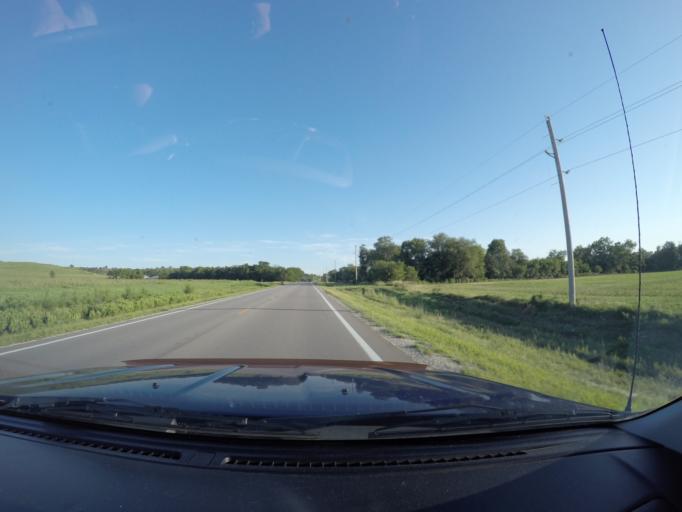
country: US
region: Kansas
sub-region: Pottawatomie County
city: Wamego
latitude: 39.1484
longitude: -96.3056
